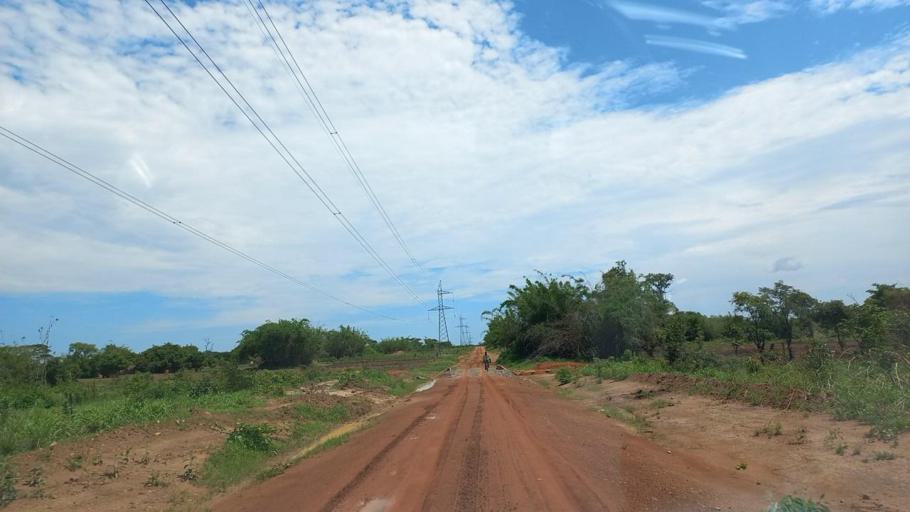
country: ZM
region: Copperbelt
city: Kitwe
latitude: -12.8236
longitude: 28.3510
